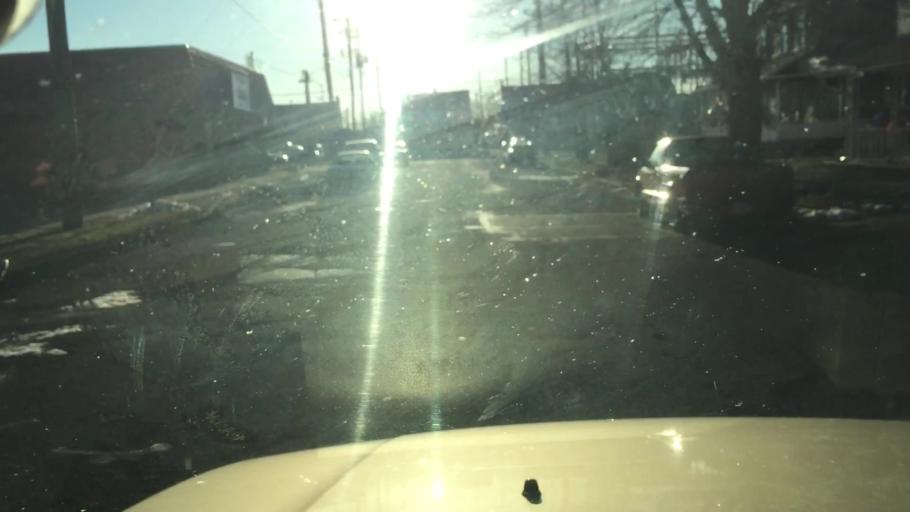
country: US
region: Pennsylvania
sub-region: Columbia County
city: Berwick
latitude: 41.0588
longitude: -76.2317
